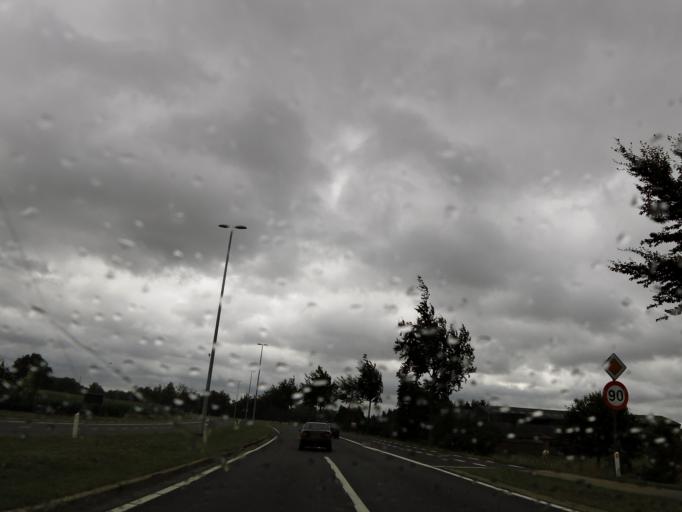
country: BE
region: Flanders
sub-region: Provincie Limburg
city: Maaseik
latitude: 51.0879
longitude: 5.7672
